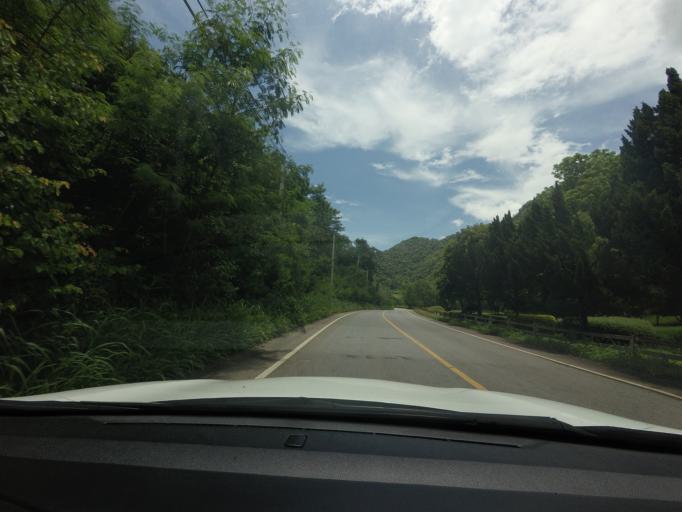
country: TH
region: Sara Buri
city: Muak Lek
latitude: 14.5730
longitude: 101.2867
